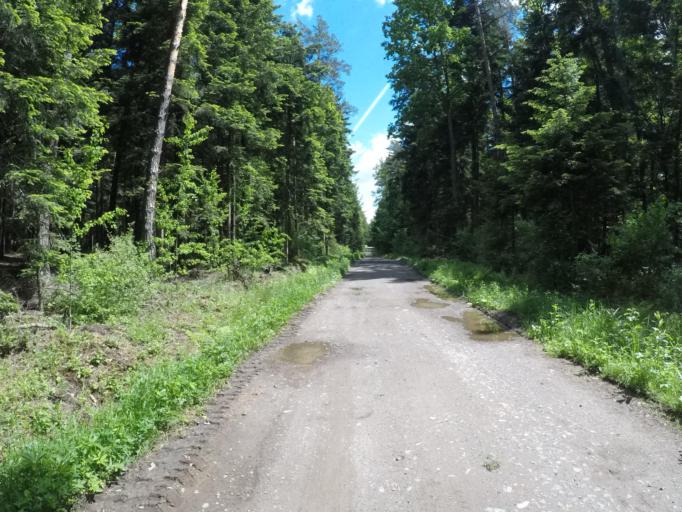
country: PL
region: Swietokrzyskie
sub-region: Powiat kielecki
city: Kostomloty Pierwsze
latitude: 50.9187
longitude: 20.6374
